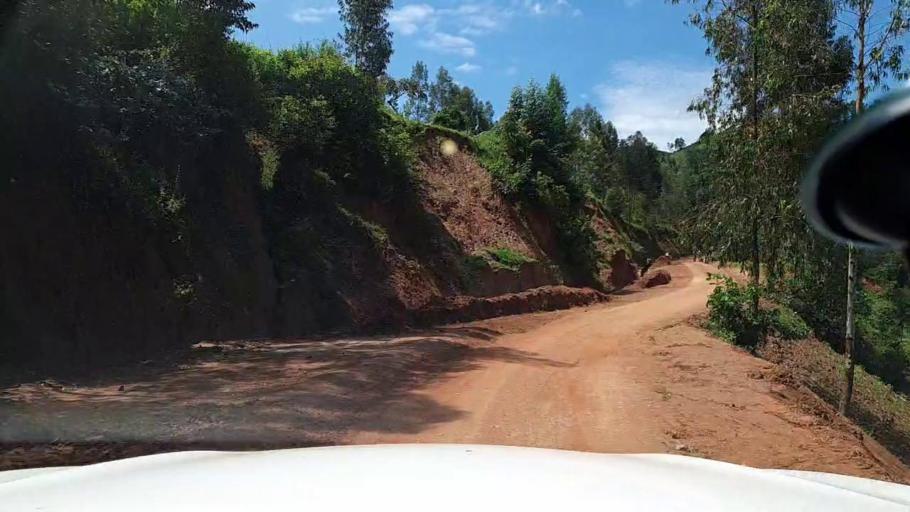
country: RW
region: Northern Province
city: Byumba
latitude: -1.7370
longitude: 29.8606
